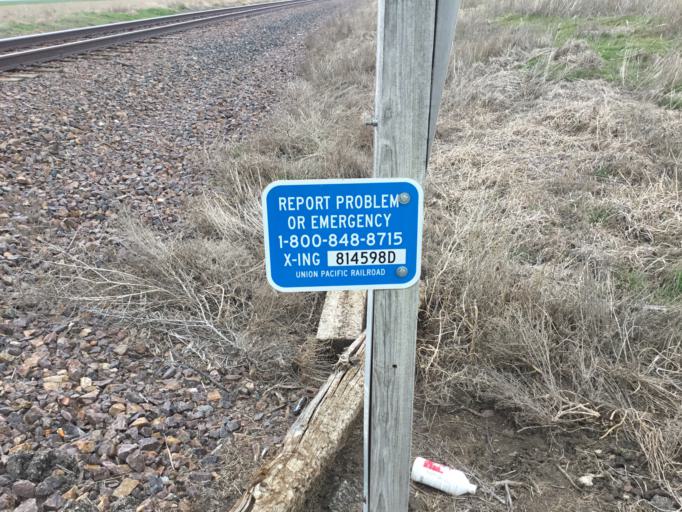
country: US
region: Kansas
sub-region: Russell County
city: Russell
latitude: 38.8901
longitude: -98.9838
